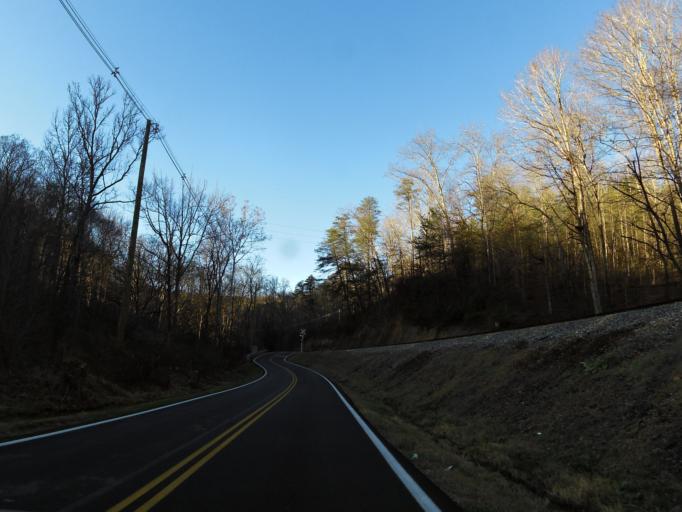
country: US
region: Tennessee
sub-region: Anderson County
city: Oak Ridge
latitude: 36.0722
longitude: -84.2471
